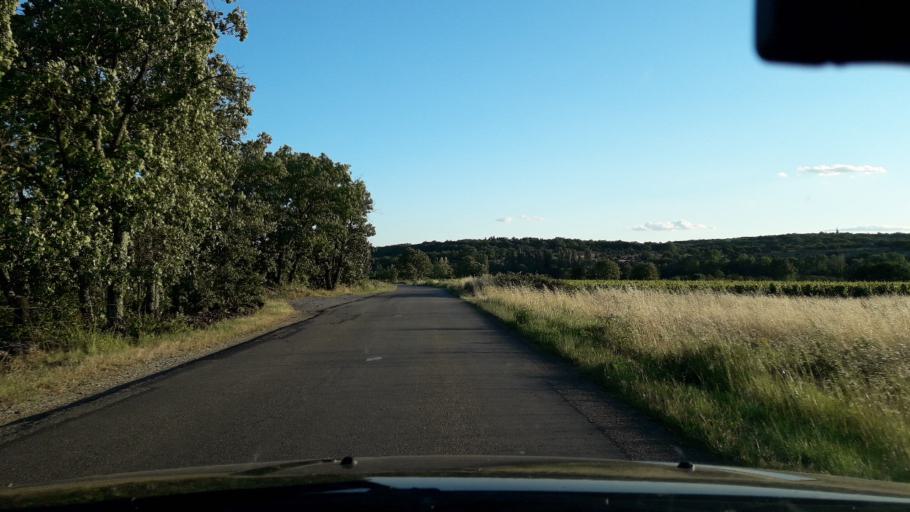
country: FR
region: Rhone-Alpes
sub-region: Departement de l'Ardeche
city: Lavilledieu
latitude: 44.5977
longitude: 4.4623
